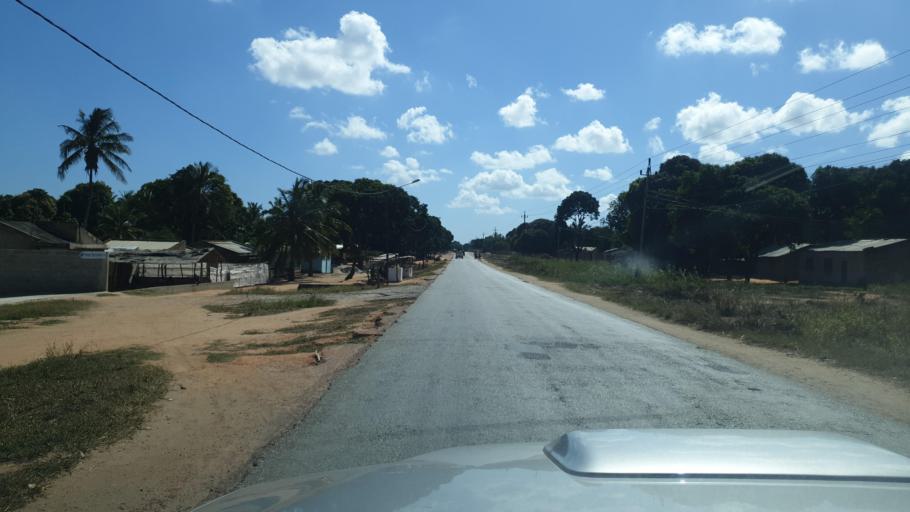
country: MZ
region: Nampula
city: Nacala
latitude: -14.5158
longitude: 40.6965
